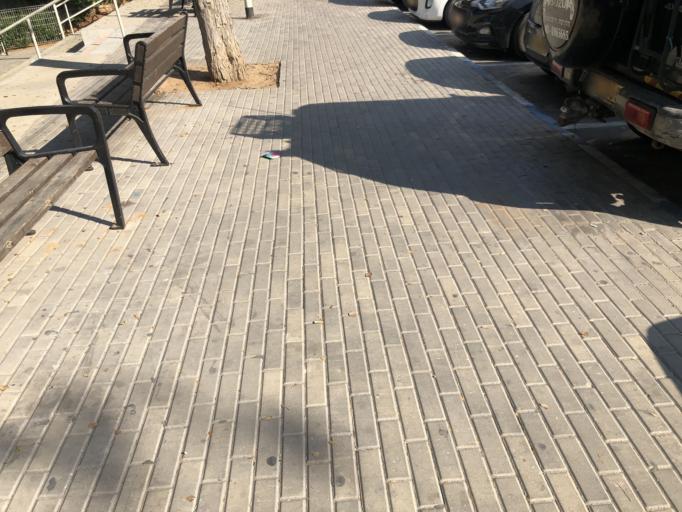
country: IL
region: Tel Aviv
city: Giv`atayim
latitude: 32.0755
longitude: 34.8133
